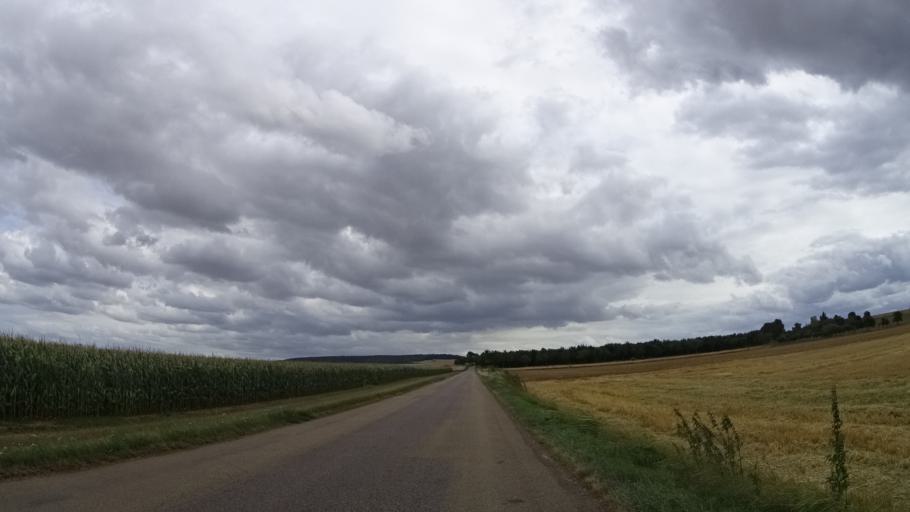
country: FR
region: Bourgogne
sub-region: Departement de l'Yonne
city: Cezy
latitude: 47.9684
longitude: 3.3558
